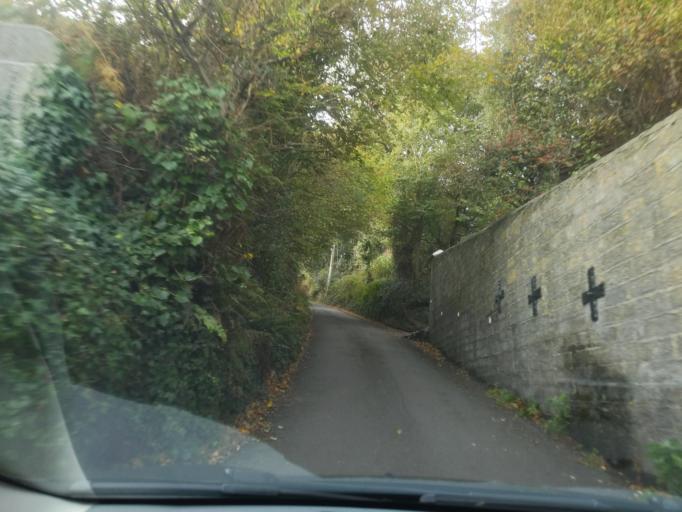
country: GB
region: England
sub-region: Cornwall
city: Looe
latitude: 50.3583
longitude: -4.4468
